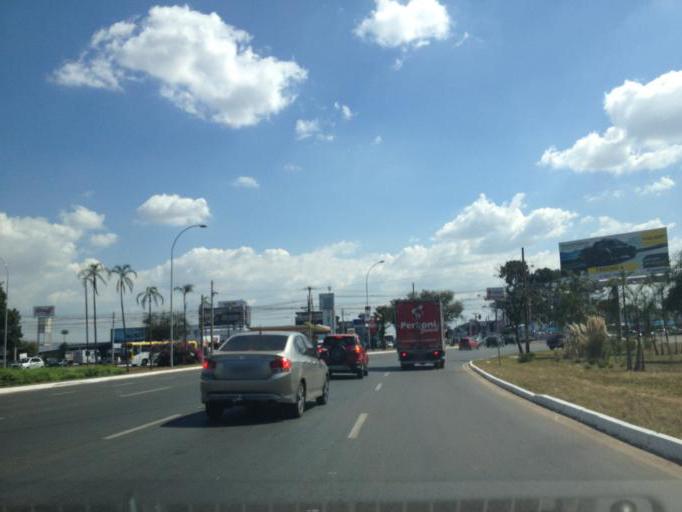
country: BR
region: Federal District
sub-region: Brasilia
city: Brasilia
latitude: -15.8077
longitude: -47.9505
